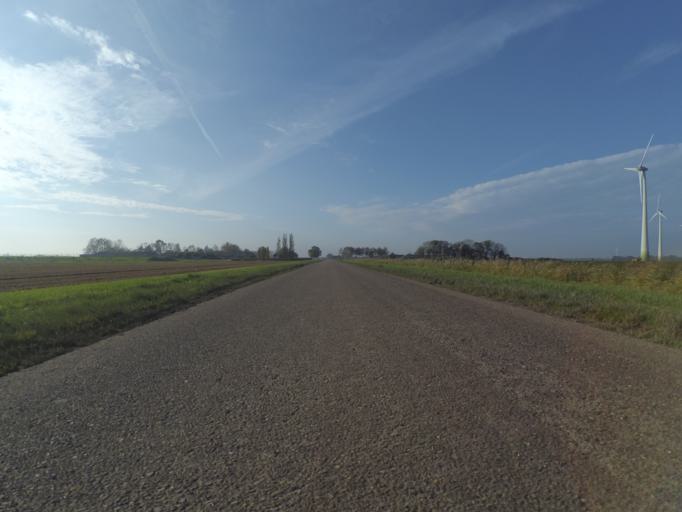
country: NL
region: Flevoland
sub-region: Gemeente Zeewolde
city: Zeewolde
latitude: 52.3795
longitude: 5.5702
